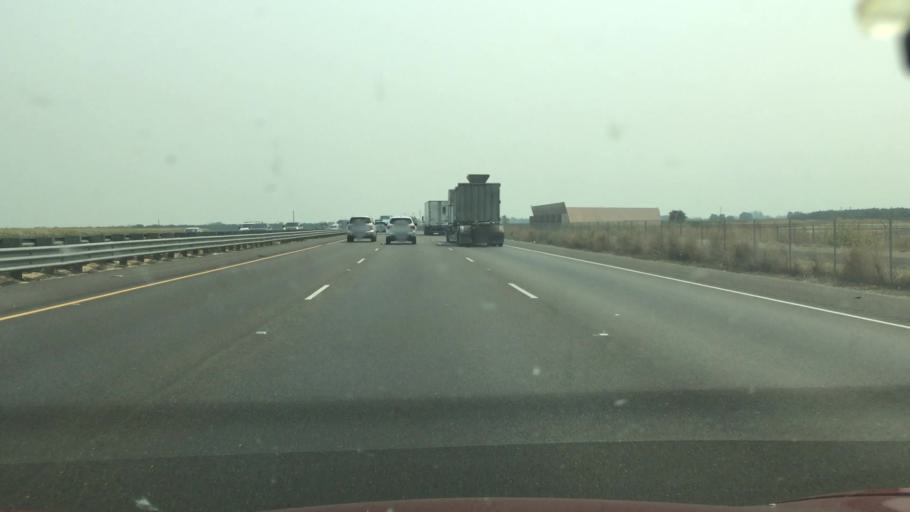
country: US
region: California
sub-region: San Joaquin County
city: French Camp
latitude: 37.8859
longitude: -121.2204
